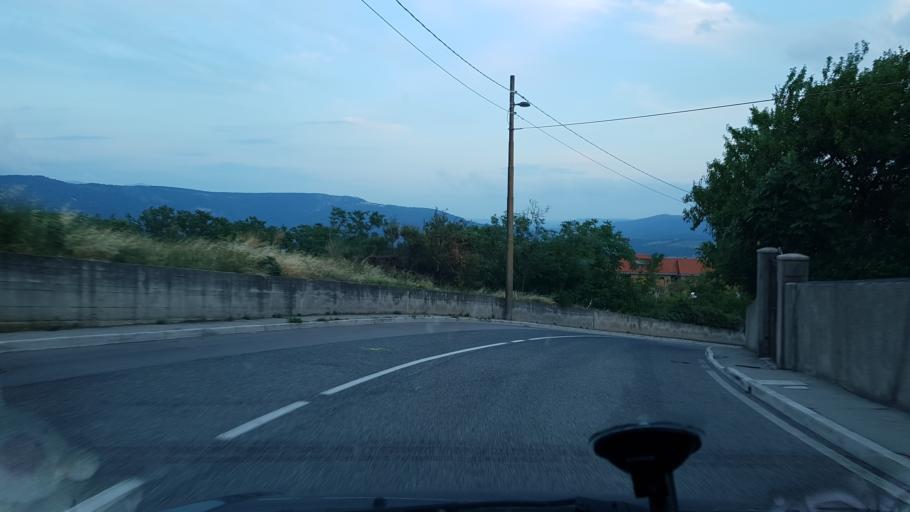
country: IT
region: Friuli Venezia Giulia
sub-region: Provincia di Trieste
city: Domio
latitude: 45.6325
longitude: 13.8231
